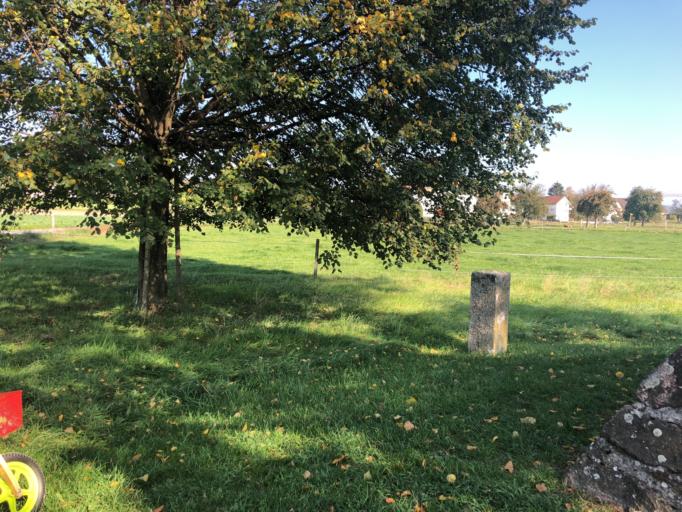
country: CH
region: Zurich
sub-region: Bezirk Uster
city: Nanikon
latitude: 47.3725
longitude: 8.6873
